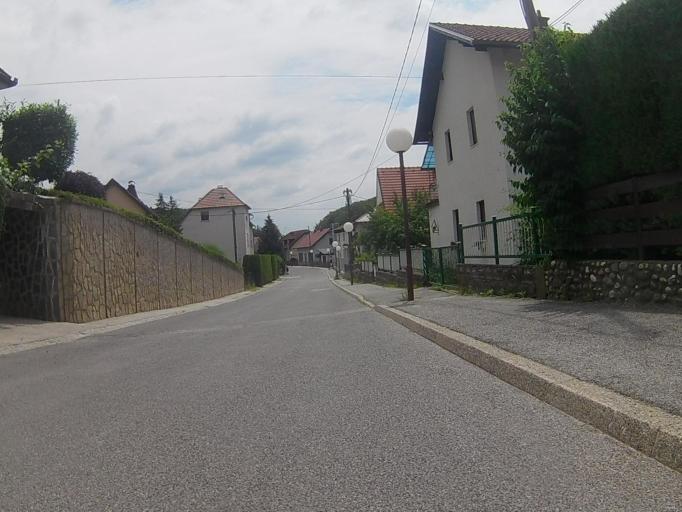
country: SI
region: Maribor
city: Maribor
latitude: 46.5747
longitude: 15.6431
